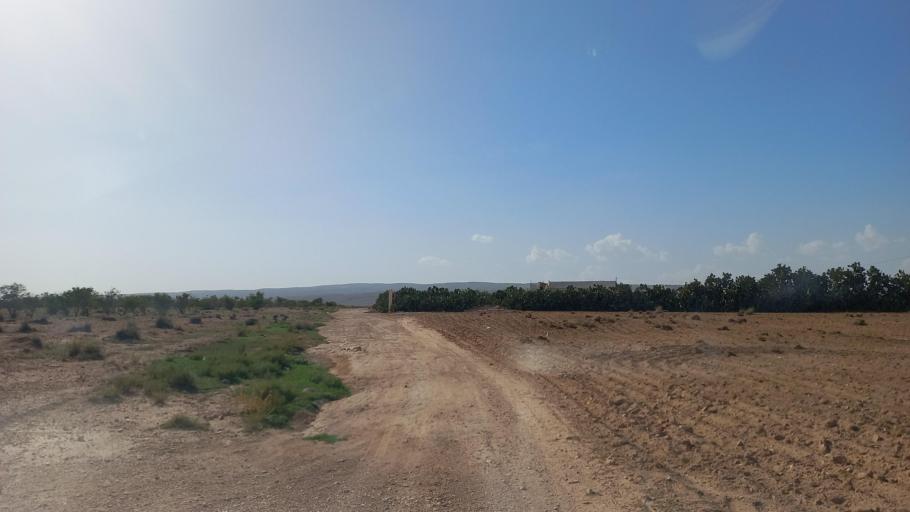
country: TN
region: Al Qasrayn
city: Kasserine
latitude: 35.3137
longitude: 9.0121
